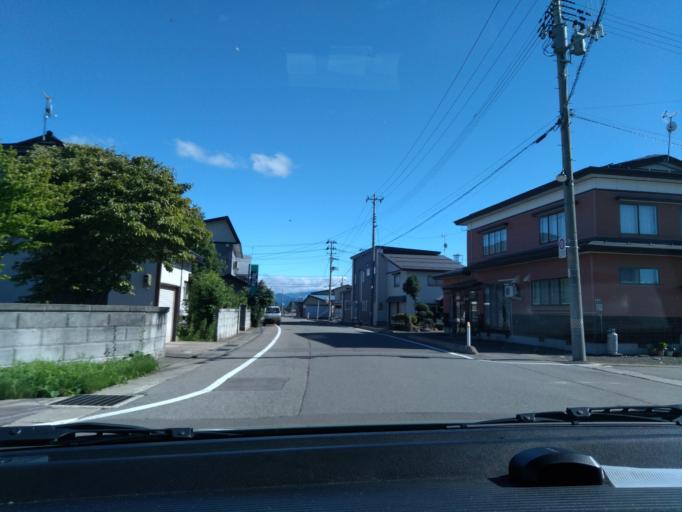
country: JP
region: Akita
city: Yuzawa
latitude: 39.2032
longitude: 140.5513
